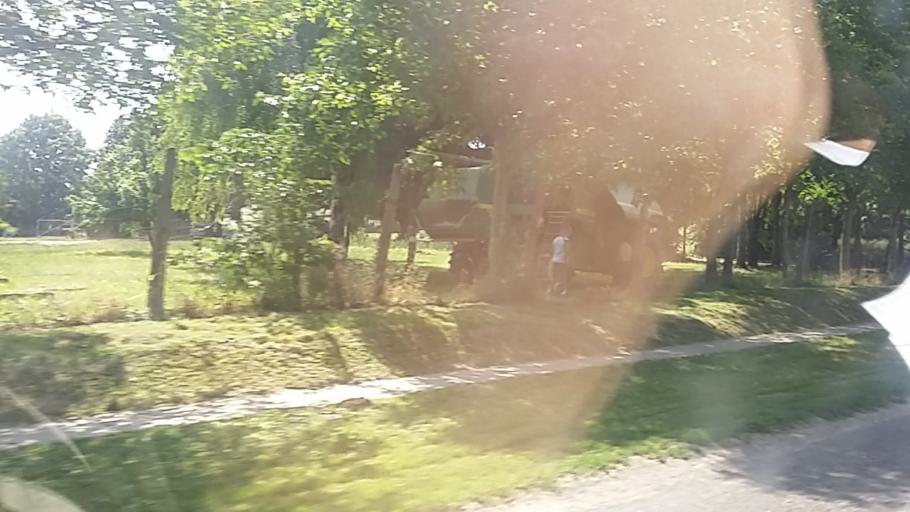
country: HU
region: Baranya
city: Siklos
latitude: 45.9020
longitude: 18.3323
